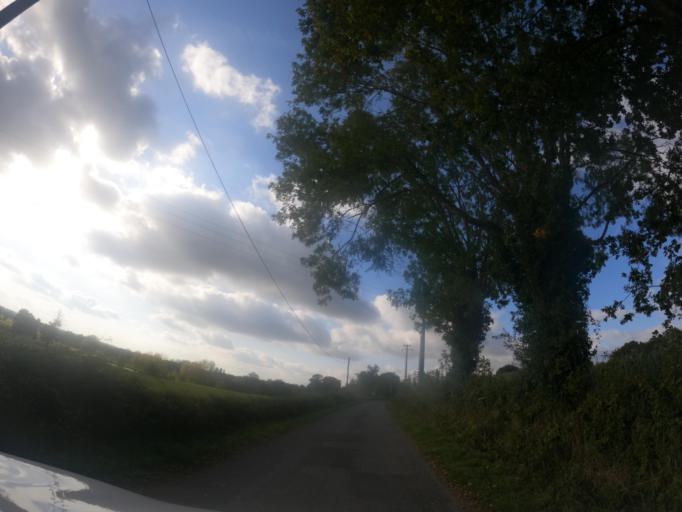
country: FR
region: Poitou-Charentes
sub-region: Departement des Deux-Sevres
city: La Foret-sur-Sevre
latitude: 46.7774
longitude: -0.6134
